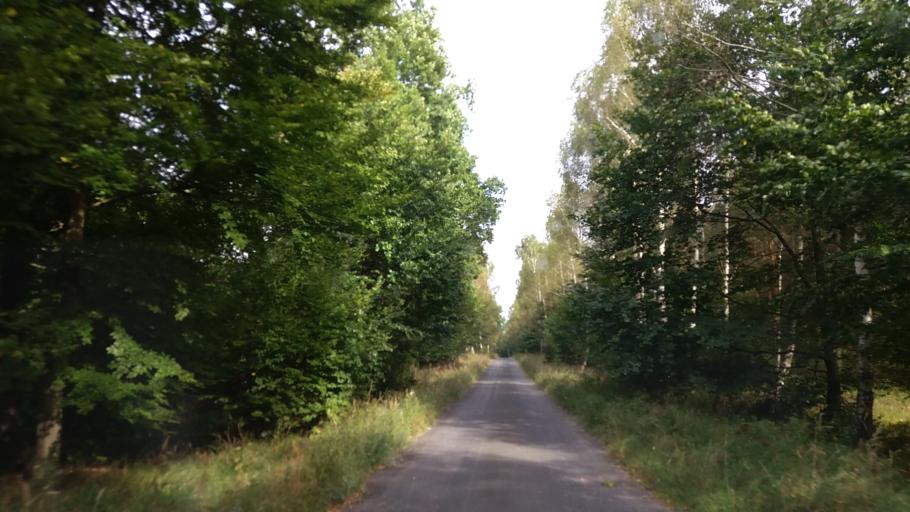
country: PL
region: West Pomeranian Voivodeship
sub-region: Powiat choszczenski
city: Krzecin
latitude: 52.9980
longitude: 15.4918
